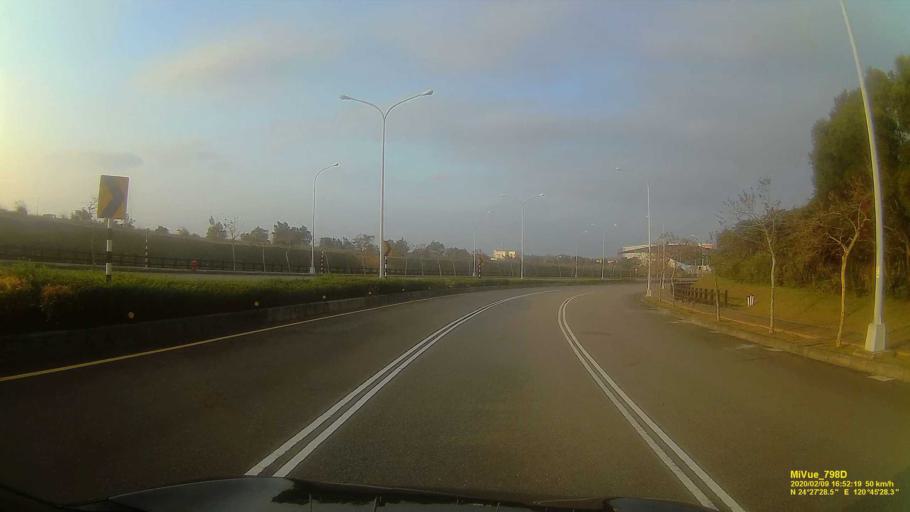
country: TW
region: Taiwan
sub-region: Miaoli
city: Miaoli
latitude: 24.4585
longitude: 120.7578
